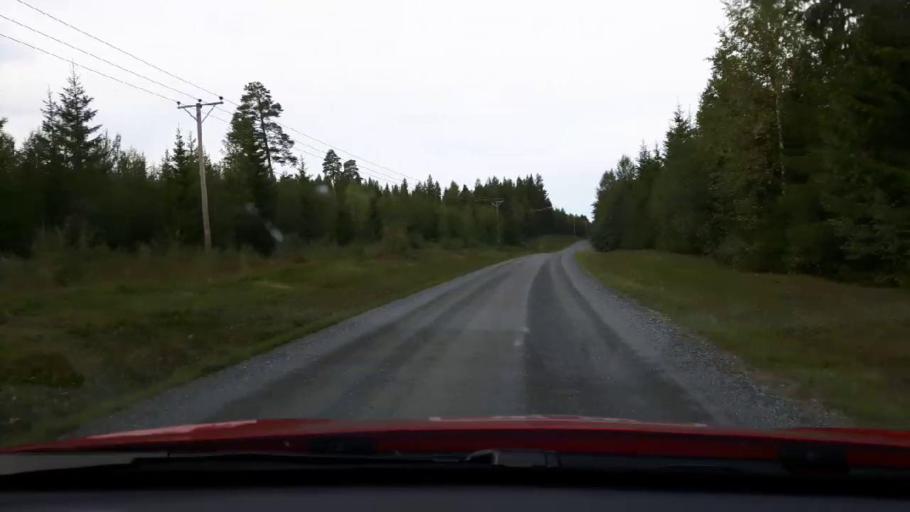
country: SE
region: Jaemtland
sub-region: Krokoms Kommun
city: Valla
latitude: 63.2458
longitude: 13.9672
